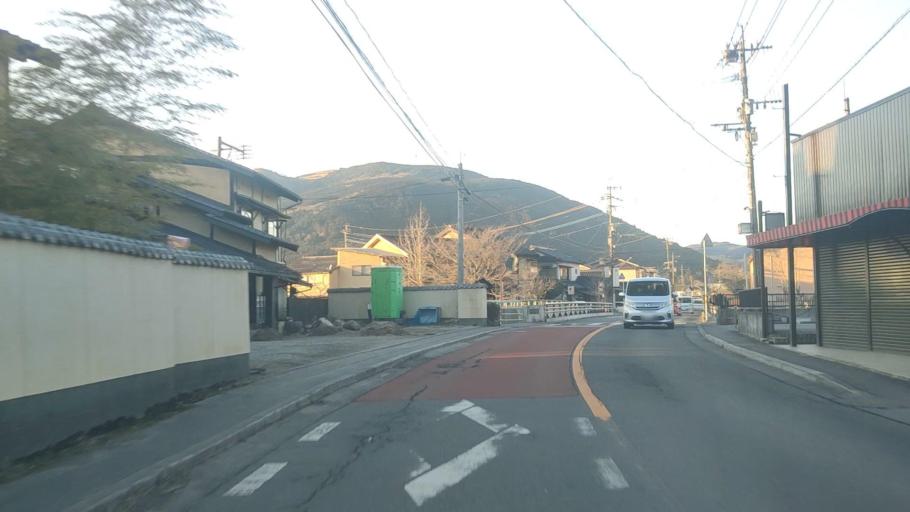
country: JP
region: Oita
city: Beppu
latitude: 33.2577
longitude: 131.3571
